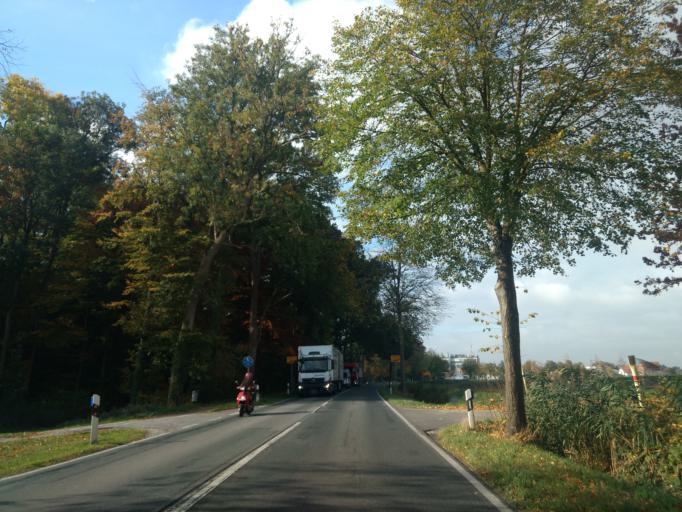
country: DE
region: Lower Saxony
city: Hilter
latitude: 52.1369
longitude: 8.1368
